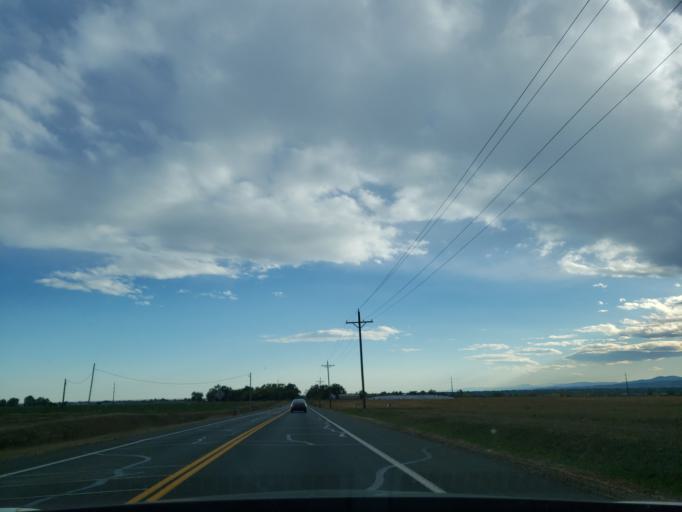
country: US
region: Colorado
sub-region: Larimer County
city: Fort Collins
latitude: 40.6092
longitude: -105.0293
